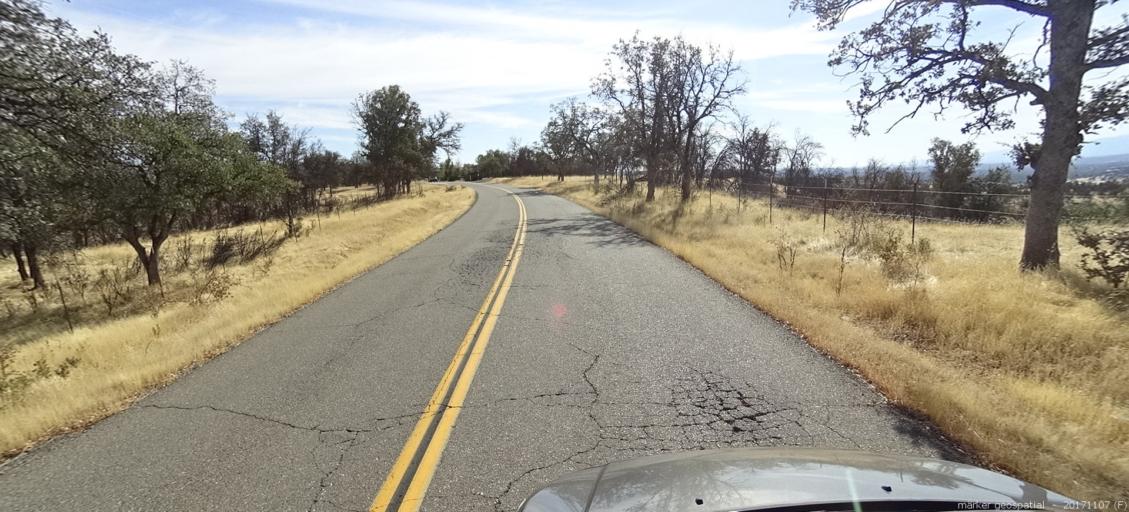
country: US
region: California
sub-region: Shasta County
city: Shasta
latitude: 40.4573
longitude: -122.5379
